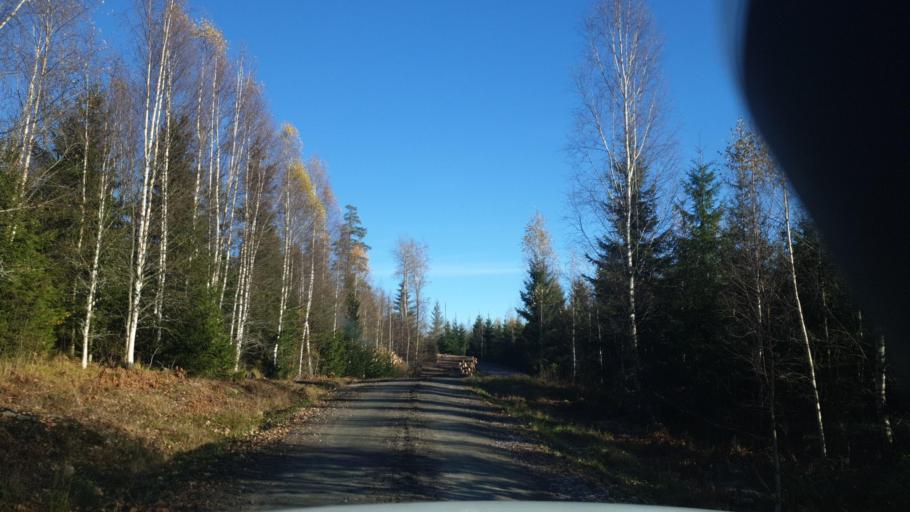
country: SE
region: Vaermland
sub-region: Karlstads Kommun
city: Edsvalla
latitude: 59.4746
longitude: 13.1285
